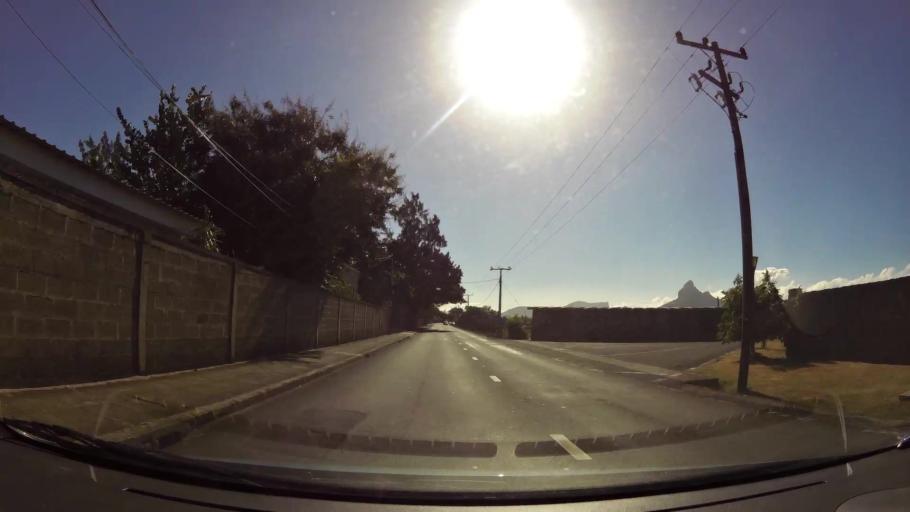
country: MU
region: Black River
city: Tamarin
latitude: -20.3359
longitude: 57.3658
